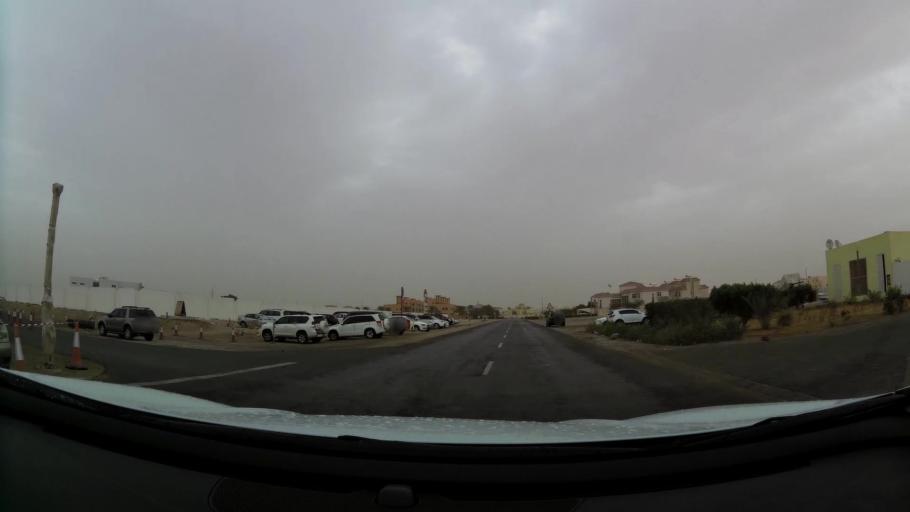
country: AE
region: Abu Dhabi
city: Abu Dhabi
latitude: 24.4287
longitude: 54.5854
